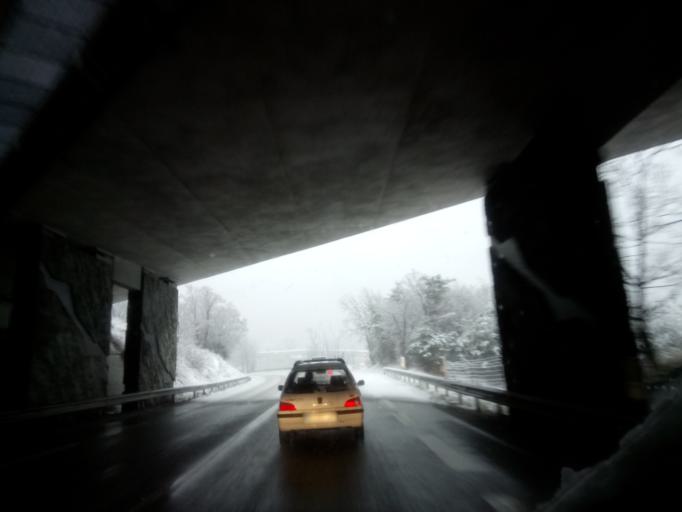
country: FR
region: Rhone-Alpes
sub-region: Departement de la Savoie
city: Saint-Michel-de-Maurienne
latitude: 45.2385
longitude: 6.4363
